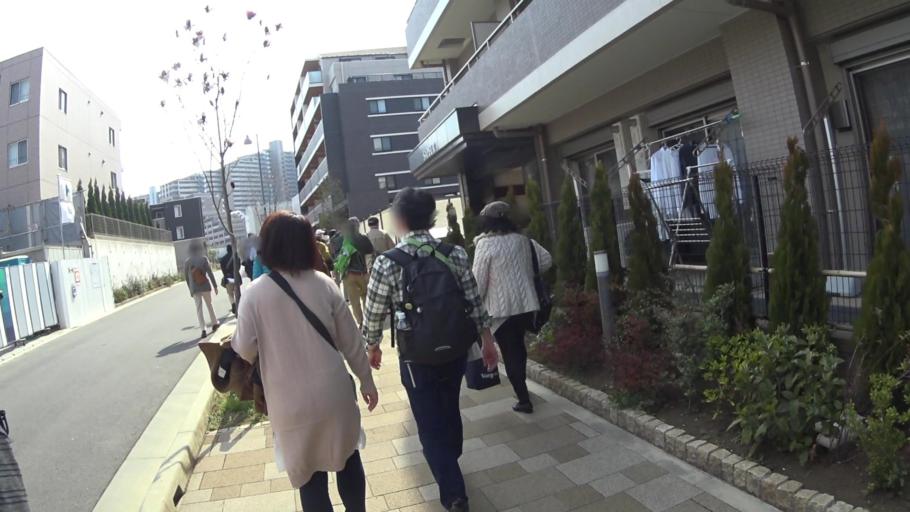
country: JP
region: Chiba
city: Funabashi
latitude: 35.6922
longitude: 140.0159
